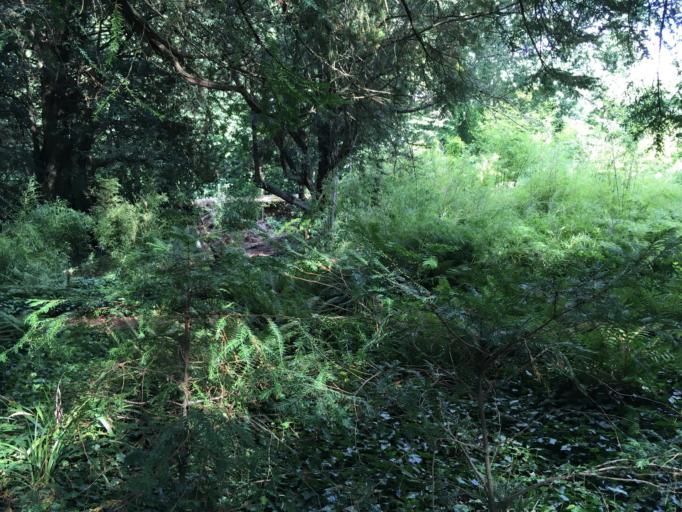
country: IE
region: Munster
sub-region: County Cork
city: Youghal
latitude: 52.1392
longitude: -7.9319
